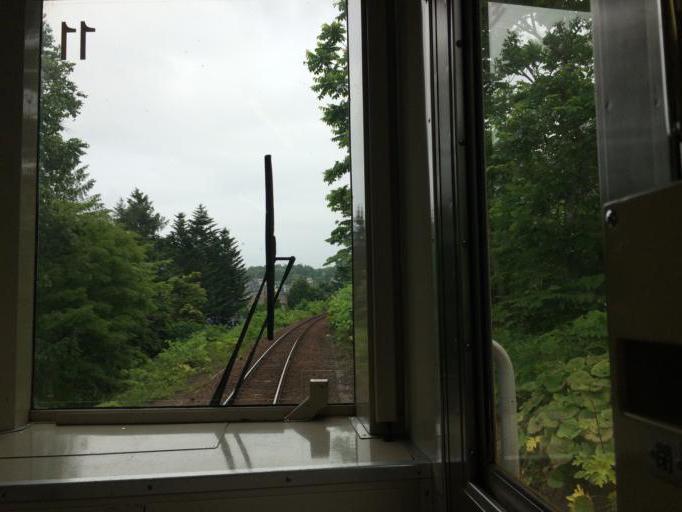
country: JP
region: Hokkaido
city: Otaru
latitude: 43.2082
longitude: 140.9752
